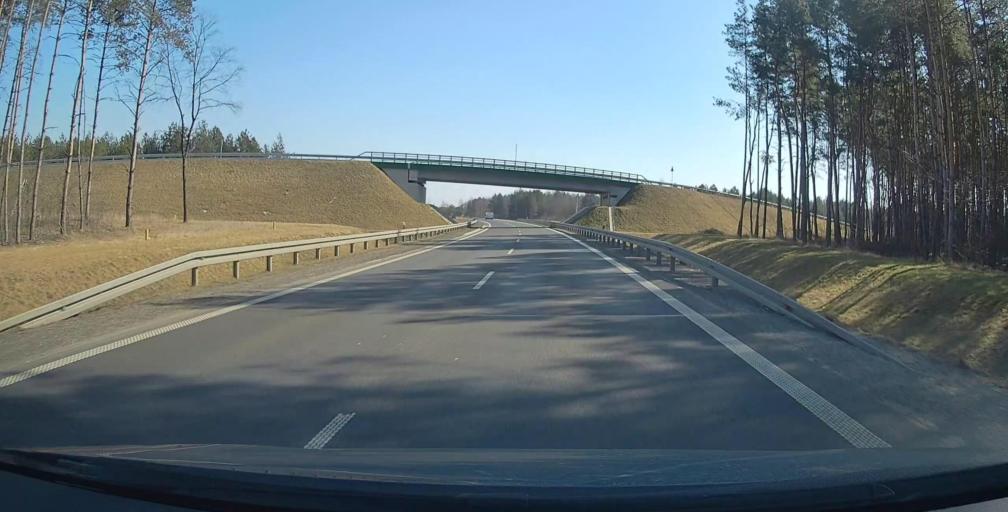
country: PL
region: Subcarpathian Voivodeship
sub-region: Powiat nizanski
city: Raclawice
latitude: 50.4960
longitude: 22.1845
